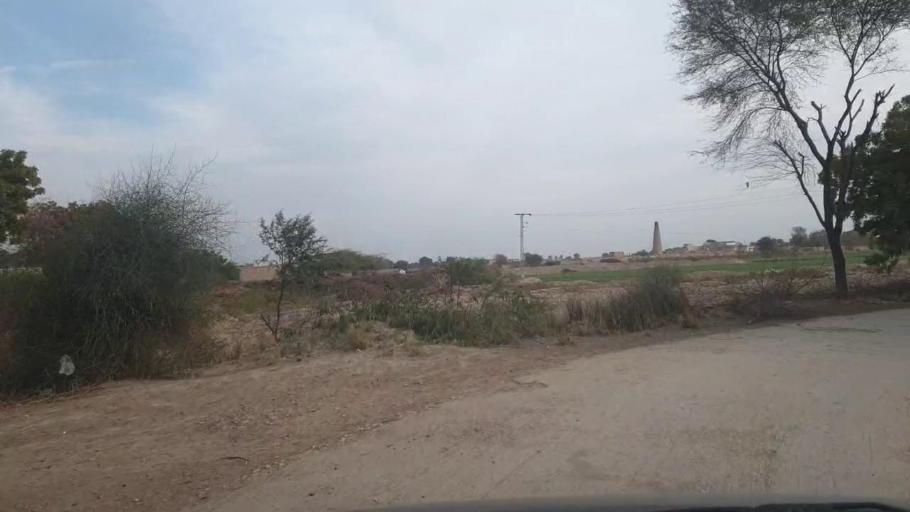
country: PK
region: Sindh
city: Shahpur Chakar
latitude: 26.1346
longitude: 68.6071
